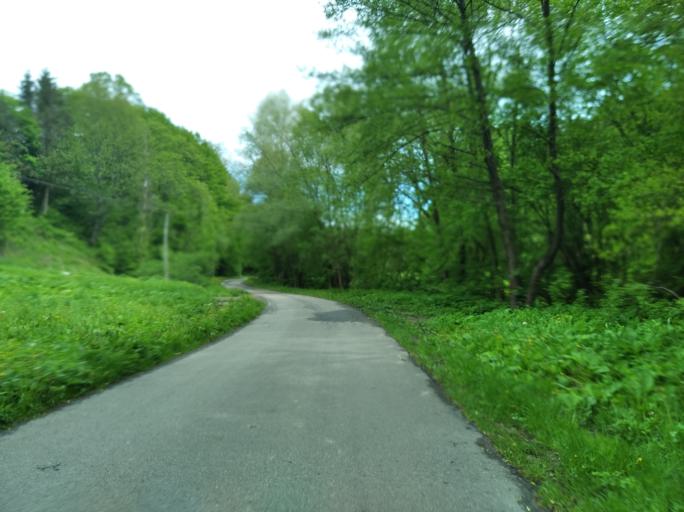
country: PL
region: Subcarpathian Voivodeship
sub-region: Powiat strzyzowski
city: Strzyzow
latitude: 49.9231
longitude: 21.7540
